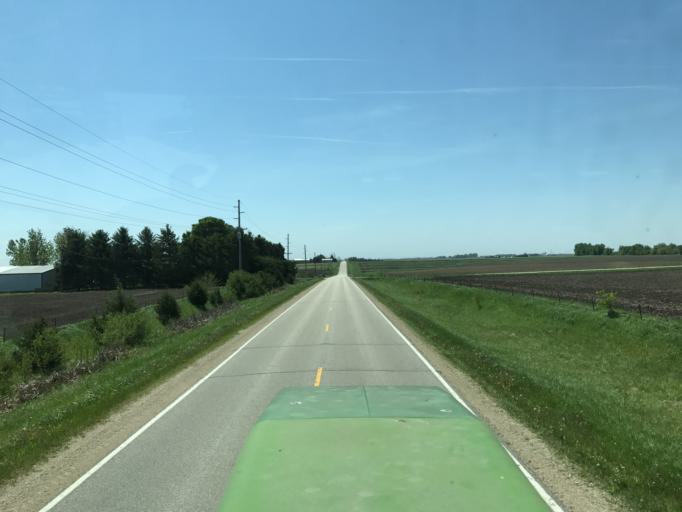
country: US
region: Iowa
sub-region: Butler County
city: Shell Rock
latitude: 42.6732
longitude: -92.5936
